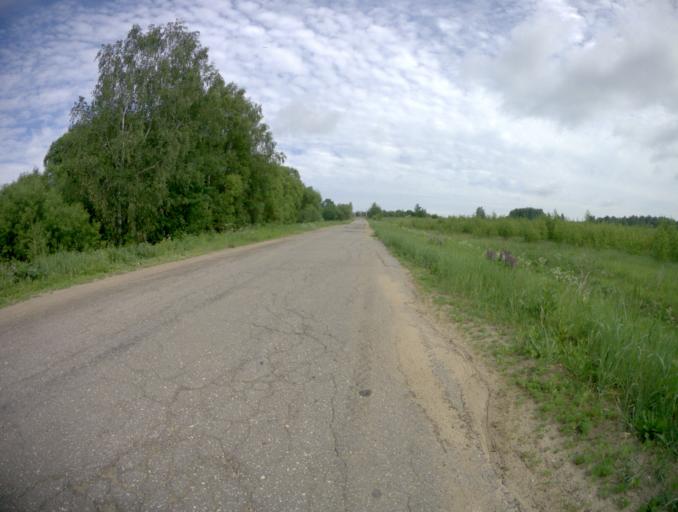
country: RU
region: Vladimir
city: Lakinsk
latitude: 56.0741
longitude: 39.8831
